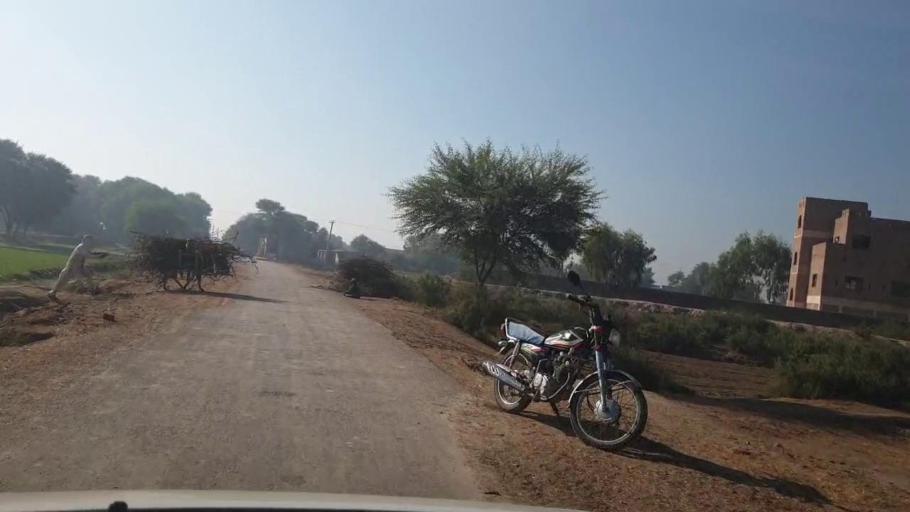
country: PK
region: Sindh
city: Dadu
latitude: 26.6503
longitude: 67.8221
